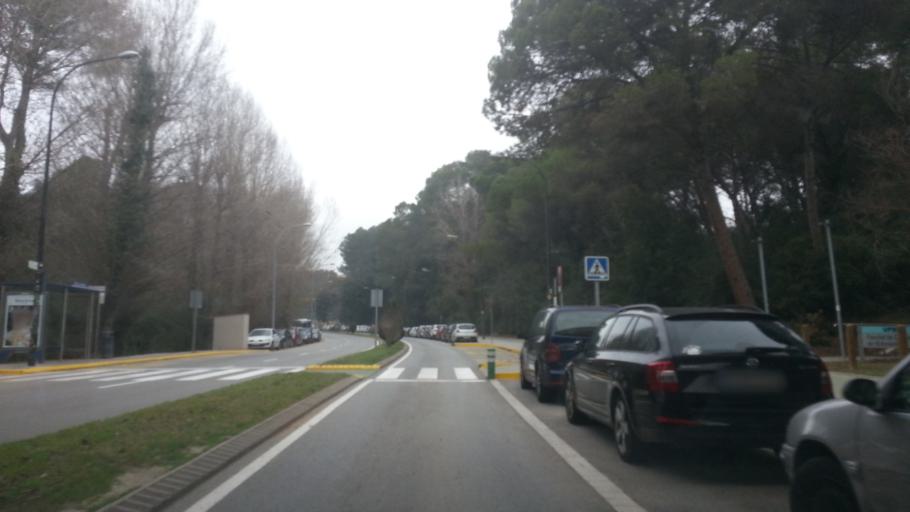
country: ES
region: Catalonia
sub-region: Provincia de Barcelona
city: Barbera del Valles
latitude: 41.5041
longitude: 2.1029
